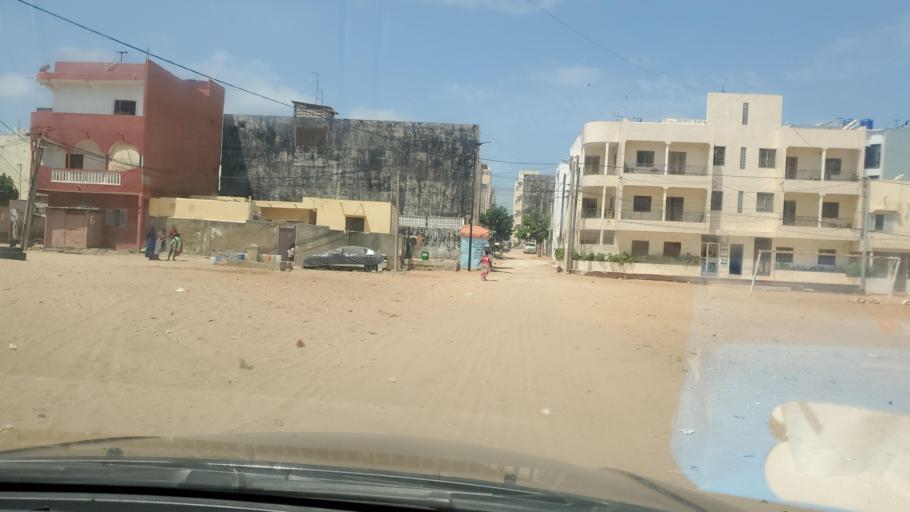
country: SN
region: Dakar
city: Grand Dakar
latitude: 14.7297
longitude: -17.4548
